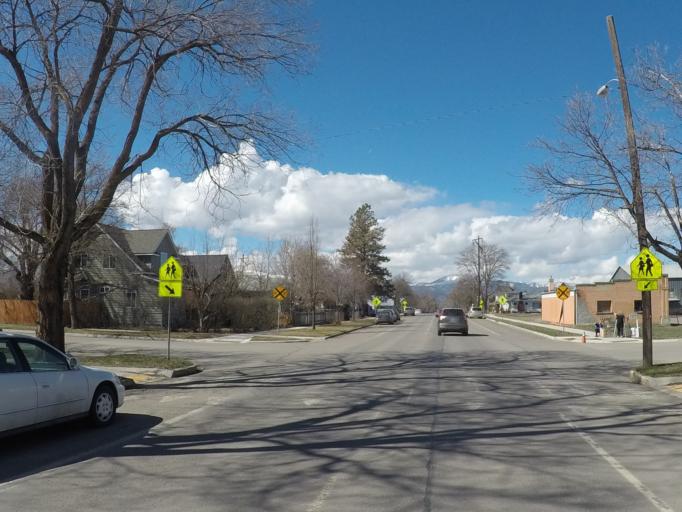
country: US
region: Montana
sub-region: Missoula County
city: Missoula
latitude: 46.8651
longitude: -114.0108
